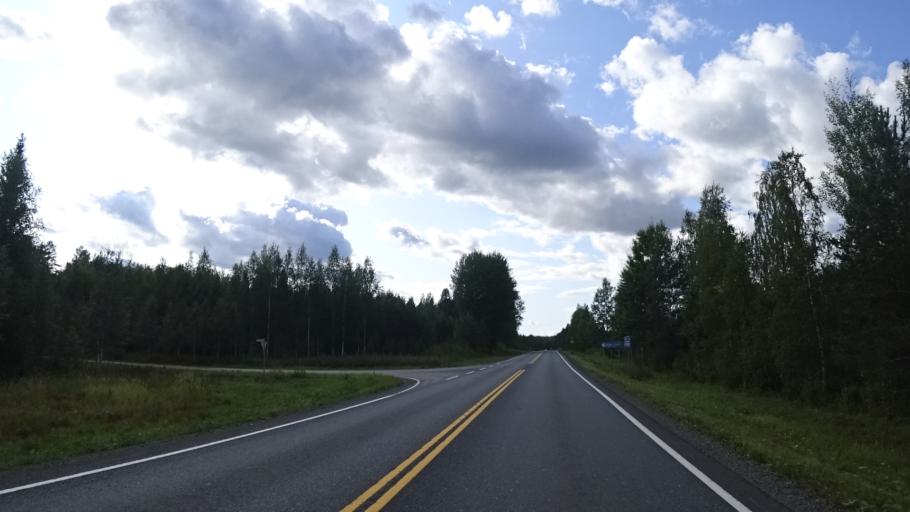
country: RU
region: Republic of Karelia
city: Vyartsilya
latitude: 62.1754
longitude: 30.5501
